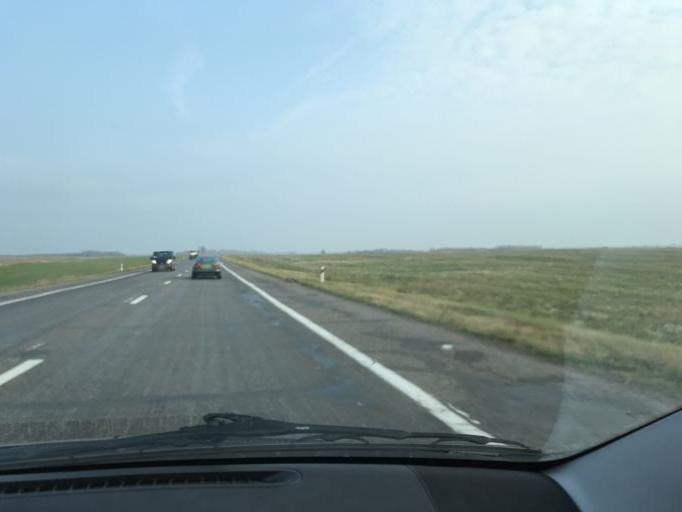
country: BY
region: Vitebsk
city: Vitebsk
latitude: 55.1519
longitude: 29.9311
